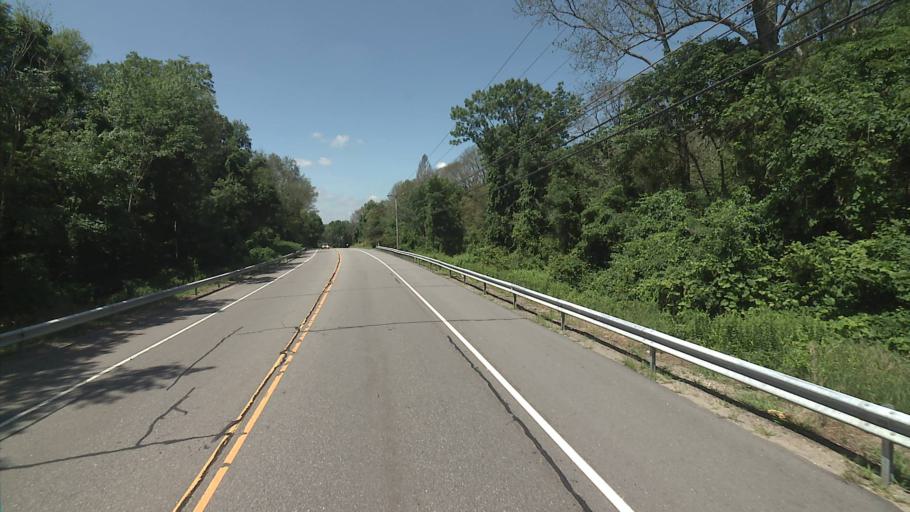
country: US
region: Connecticut
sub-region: Windham County
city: Plainfield Village
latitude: 41.6972
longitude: -71.9817
